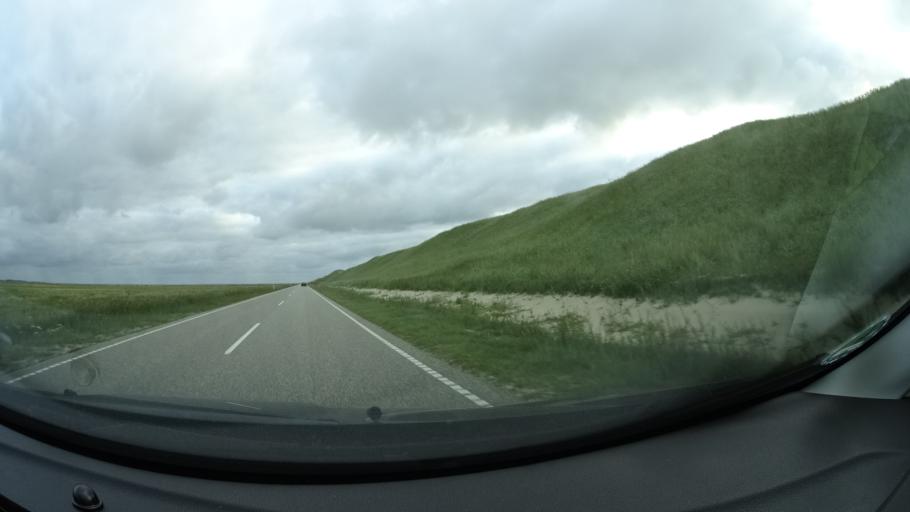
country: DK
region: Central Jutland
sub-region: Lemvig Kommune
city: Harboore
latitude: 56.4288
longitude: 8.1238
